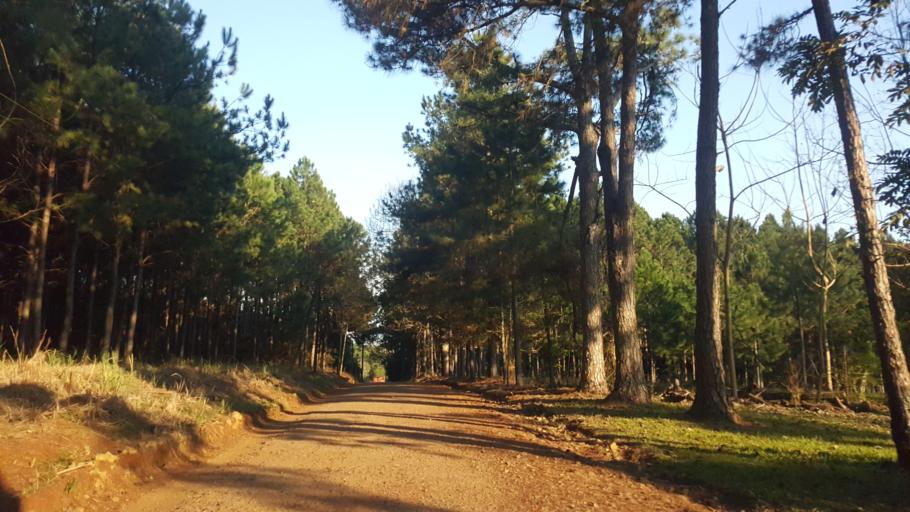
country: AR
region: Misiones
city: Capiovi
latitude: -26.8992
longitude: -55.0560
